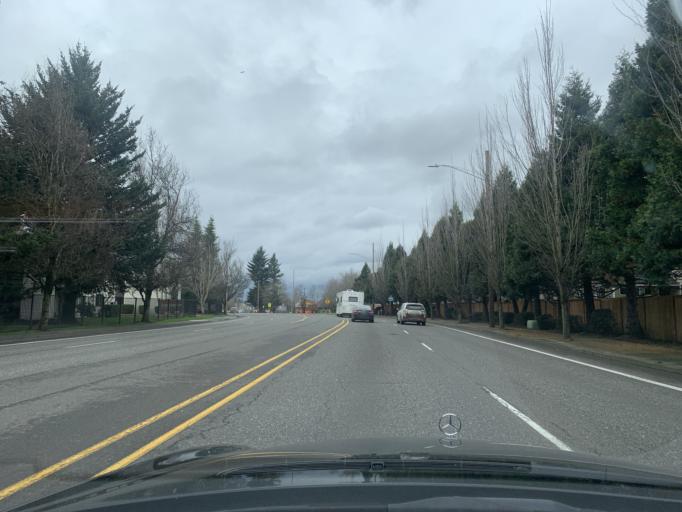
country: US
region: Oregon
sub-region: Multnomah County
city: Troutdale
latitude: 45.5268
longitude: -122.3984
